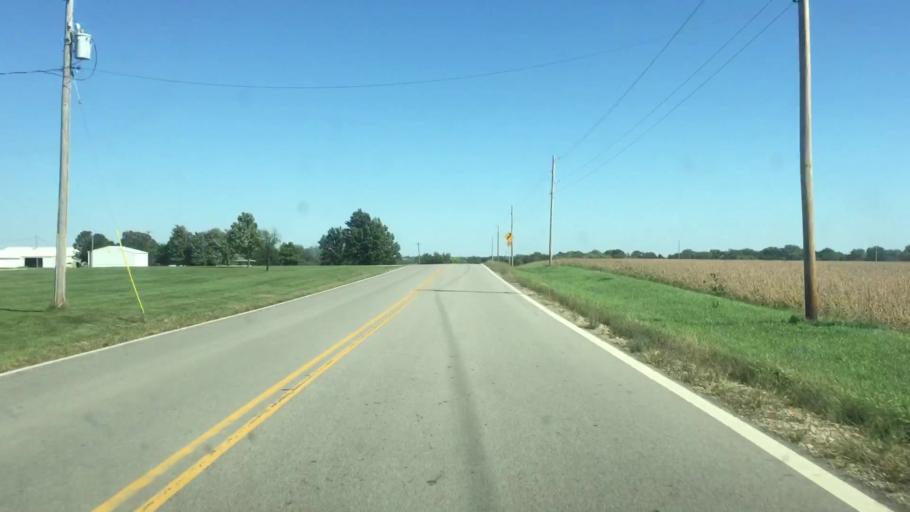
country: US
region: Kansas
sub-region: Brown County
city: Horton
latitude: 39.5949
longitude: -95.6239
